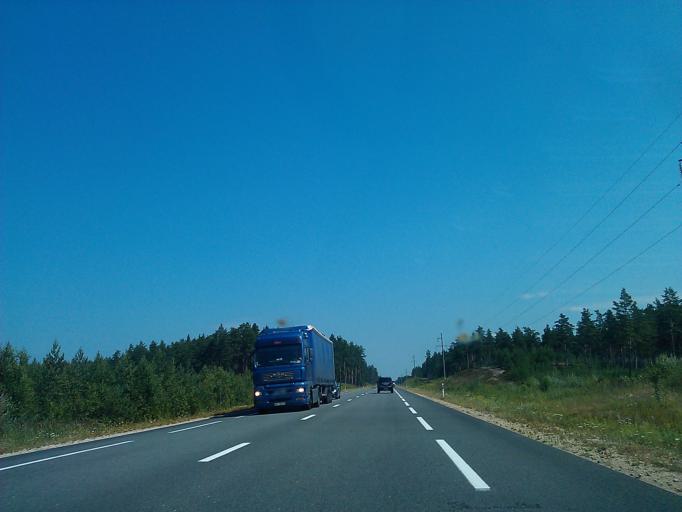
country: LV
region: Saulkrastu
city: Saulkrasti
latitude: 57.2070
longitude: 24.3854
